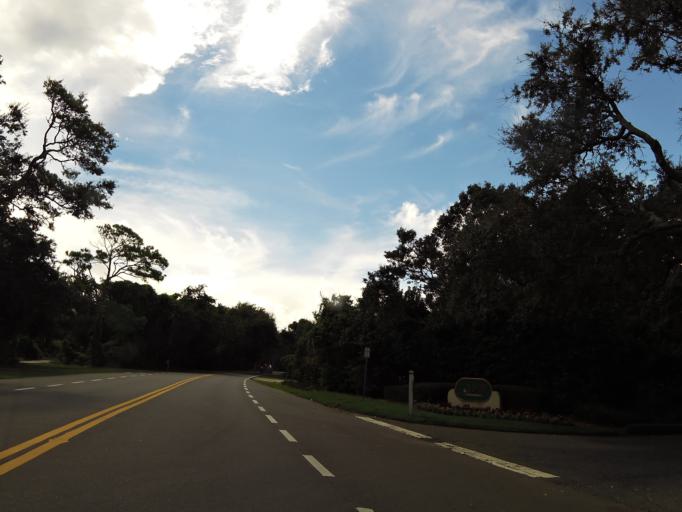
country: US
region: Florida
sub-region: Nassau County
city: Fernandina Beach
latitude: 30.5941
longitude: -81.4468
